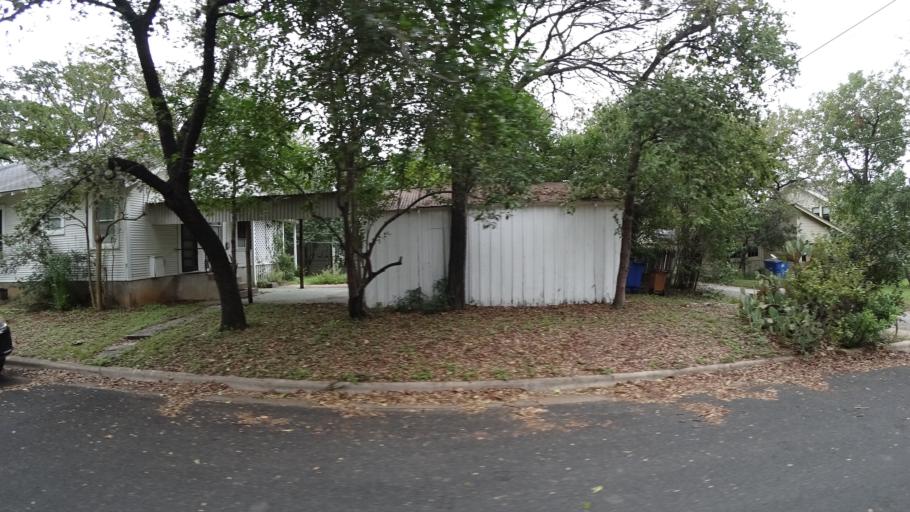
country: US
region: Texas
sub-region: Travis County
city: Austin
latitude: 30.3023
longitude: -97.7263
